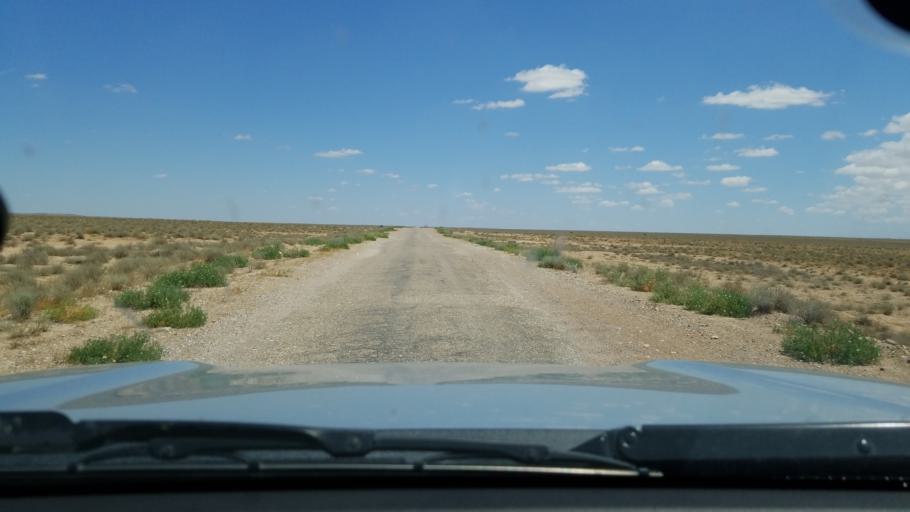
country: TM
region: Balkan
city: Turkmenbasy
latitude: 40.1427
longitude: 53.5476
